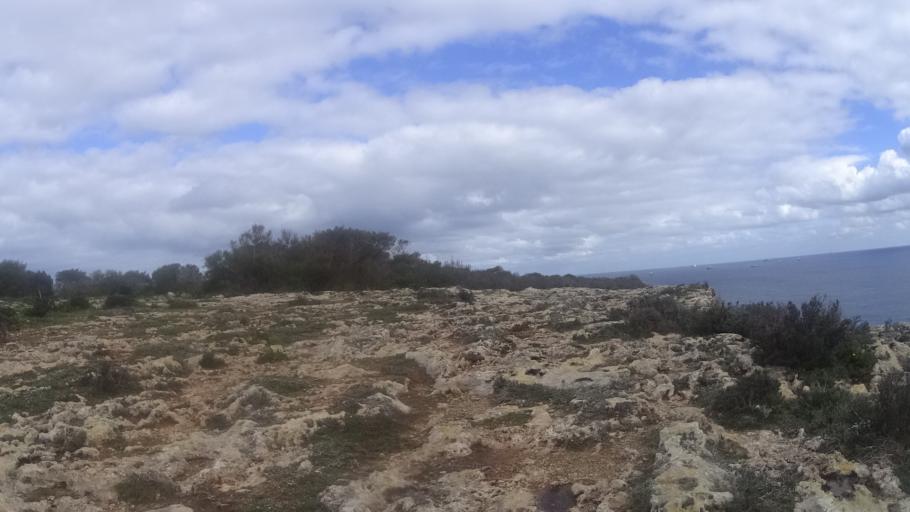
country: MT
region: Il-Mellieha
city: Mellieha
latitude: 35.9863
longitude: 14.3711
